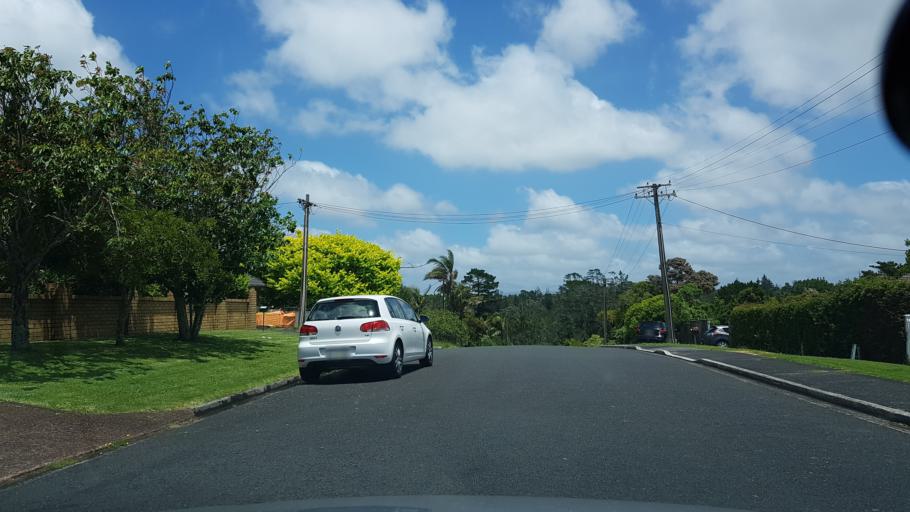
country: NZ
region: Auckland
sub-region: Auckland
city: North Shore
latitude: -36.8153
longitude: 174.7063
